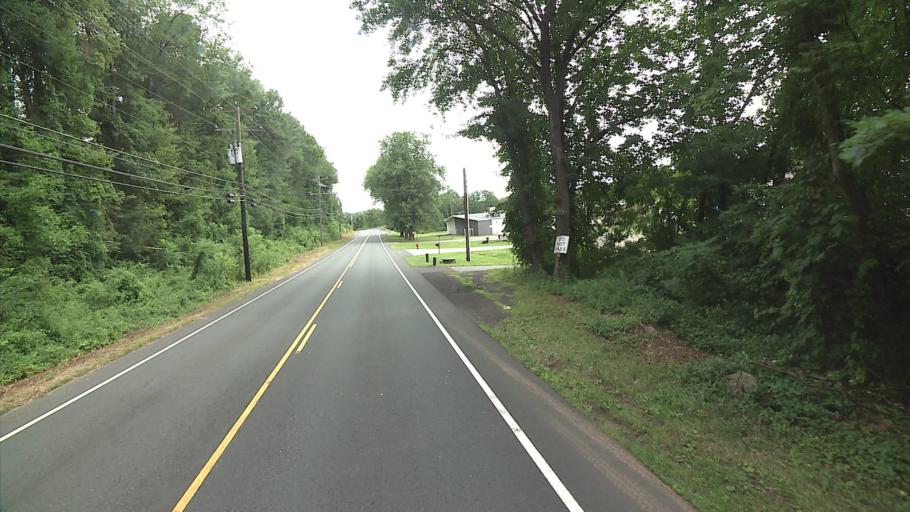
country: US
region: Connecticut
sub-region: Litchfield County
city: Winsted
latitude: 41.9510
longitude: -73.0491
